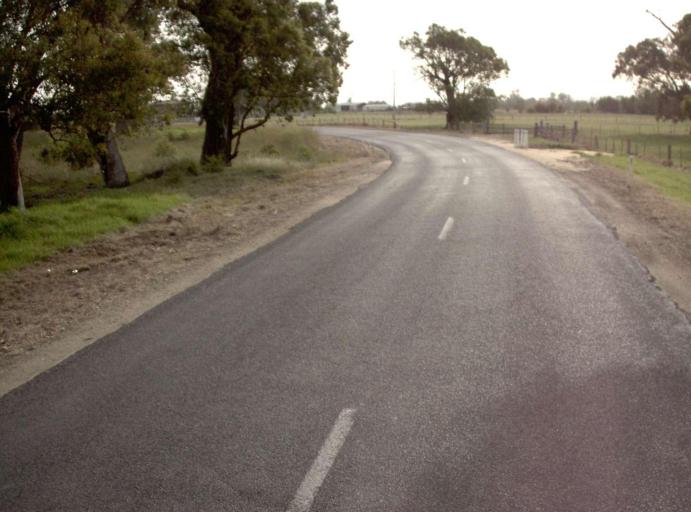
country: AU
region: Victoria
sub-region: Wellington
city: Heyfield
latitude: -37.9874
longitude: 146.7786
